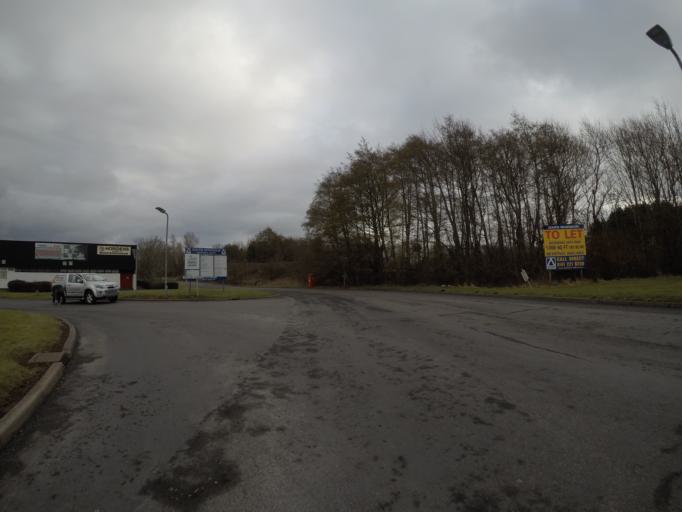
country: GB
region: Scotland
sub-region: North Ayrshire
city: Irvine
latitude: 55.6099
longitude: -4.6415
